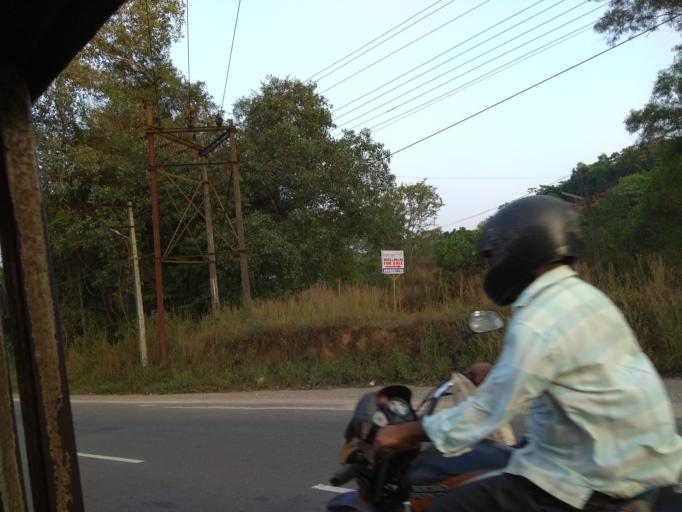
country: IN
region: Karnataka
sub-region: Dakshina Kannada
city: Mangalore
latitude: 12.9366
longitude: 74.8618
